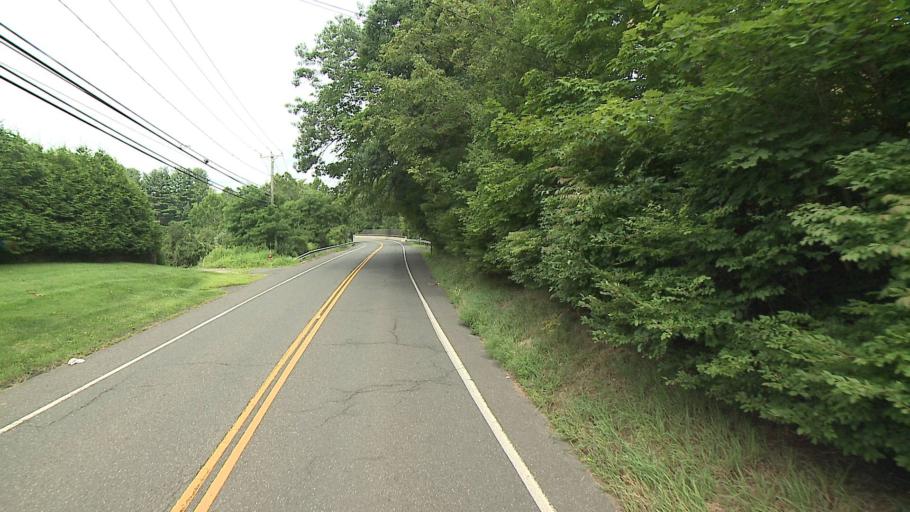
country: US
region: Connecticut
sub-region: Litchfield County
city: Woodbury
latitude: 41.5398
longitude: -73.2124
